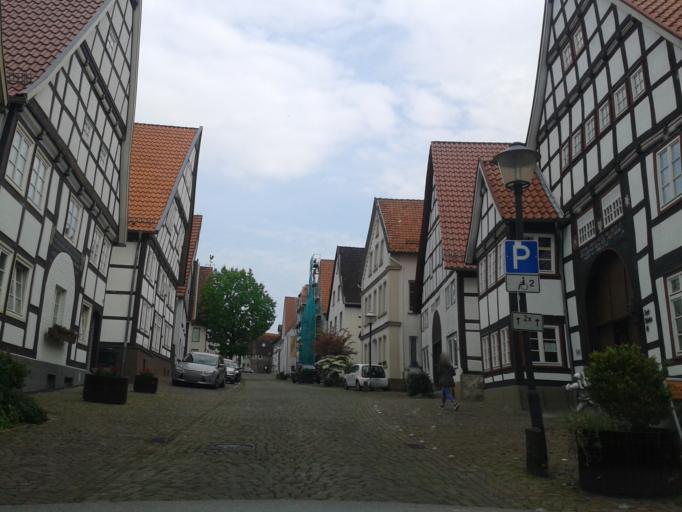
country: DE
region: North Rhine-Westphalia
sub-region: Regierungsbezirk Detmold
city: Blomberg
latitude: 51.9423
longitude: 9.0926
